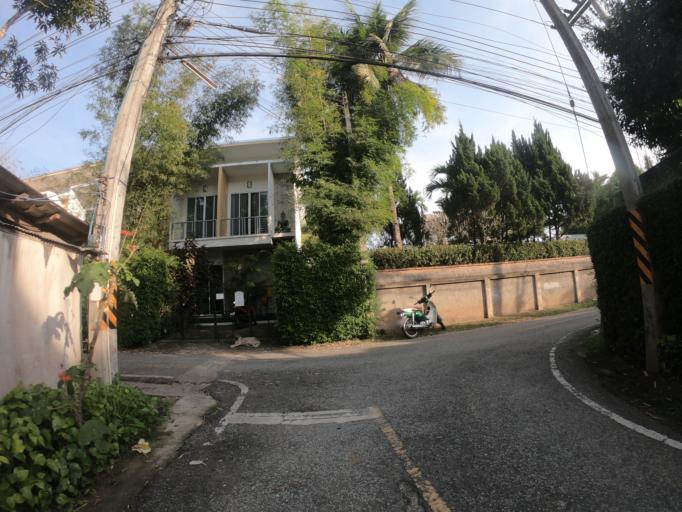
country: TH
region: Chiang Mai
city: Chiang Mai
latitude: 18.8187
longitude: 98.9551
